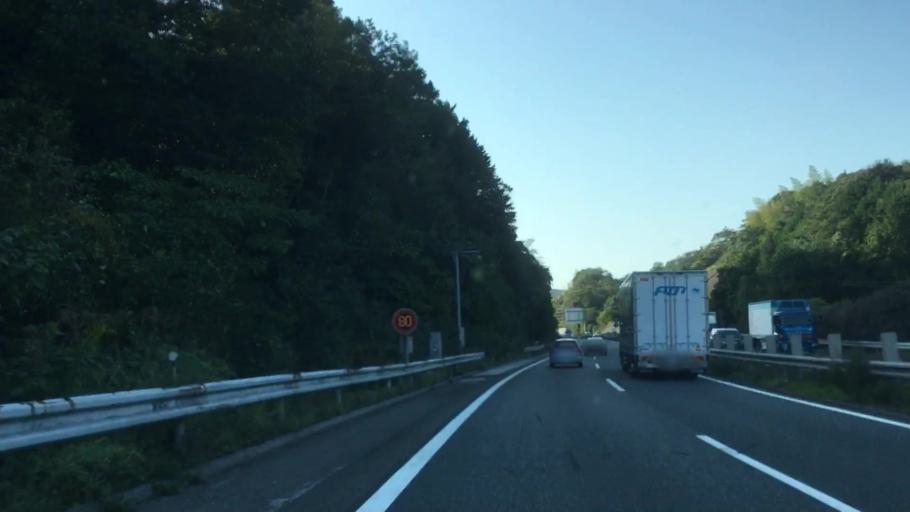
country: JP
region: Yamaguchi
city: Ogori-shimogo
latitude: 34.1272
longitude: 131.3832
